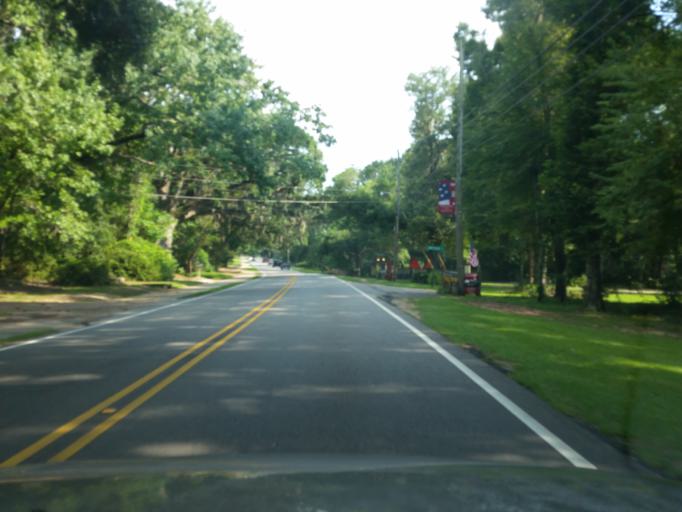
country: US
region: Alabama
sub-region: Baldwin County
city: Daphne
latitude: 30.6237
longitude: -87.9112
